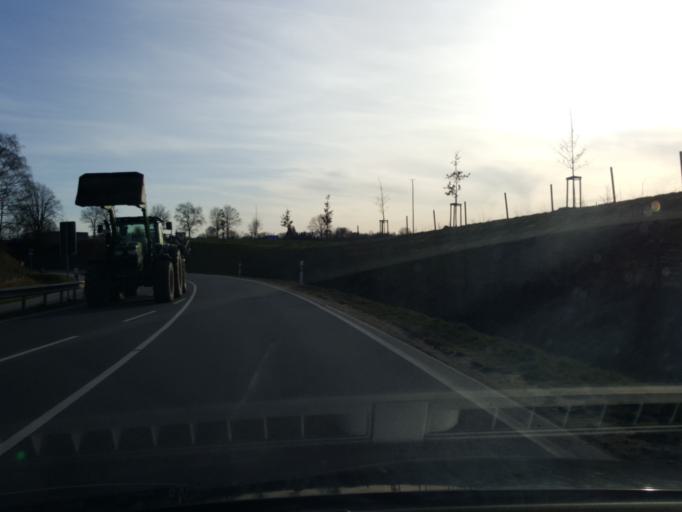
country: DE
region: Lower Saxony
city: Seevetal
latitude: 53.3808
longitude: 9.9687
